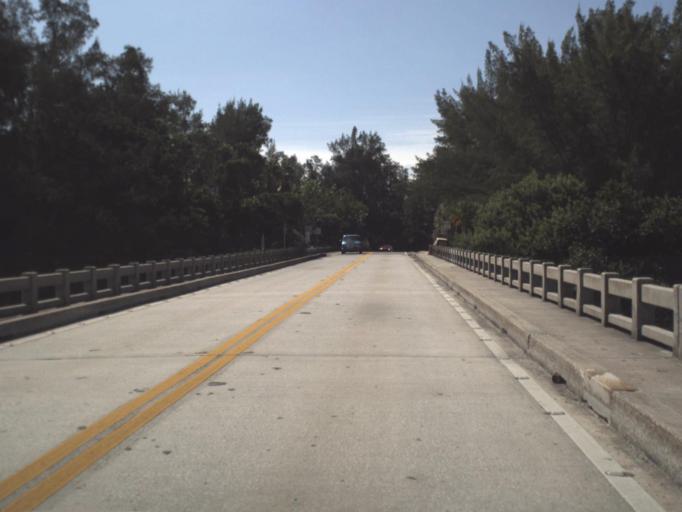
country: US
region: Florida
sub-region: Manatee County
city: Cortez
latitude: 27.4408
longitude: -82.6865
